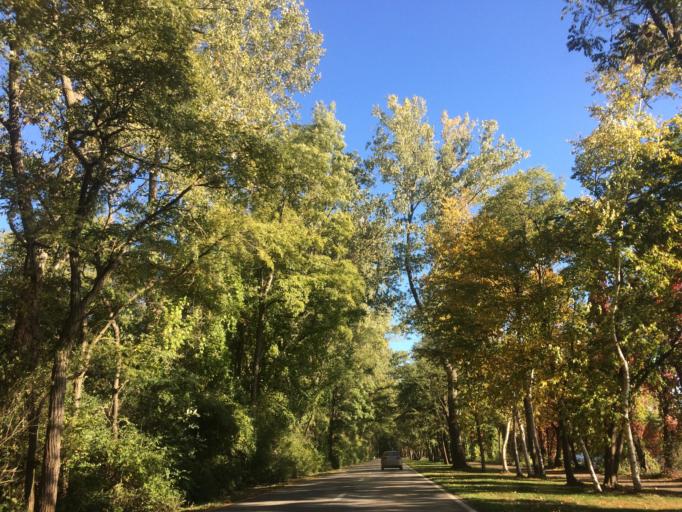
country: US
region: Pennsylvania
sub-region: Erie County
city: Erie
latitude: 42.1377
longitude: -80.1408
